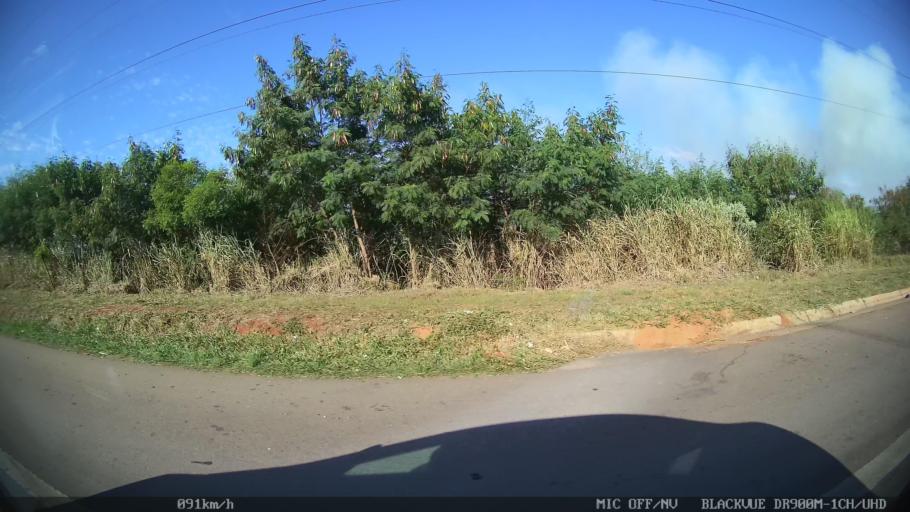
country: BR
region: Sao Paulo
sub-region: Piracicaba
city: Piracicaba
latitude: -22.6857
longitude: -47.5968
